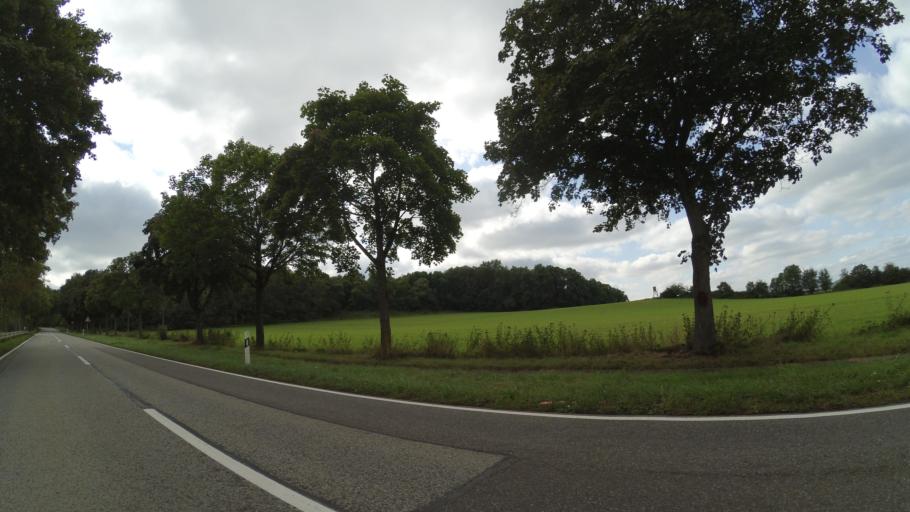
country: DE
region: Saarland
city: Uberherrn
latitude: 49.2286
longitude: 6.7035
